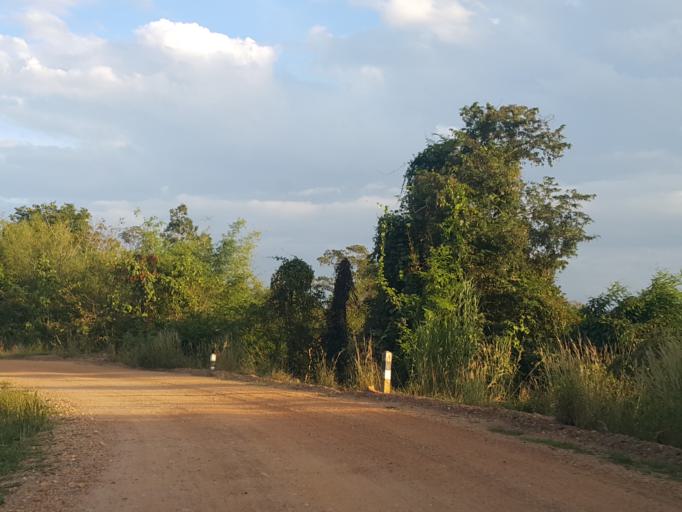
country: TH
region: Lampang
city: Mae Mo
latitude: 18.4337
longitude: 99.5974
